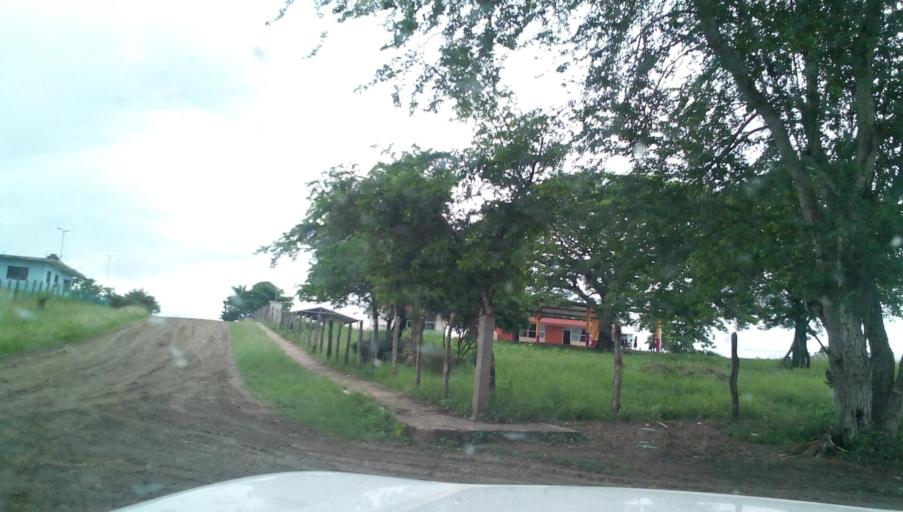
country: MX
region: Veracruz
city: Panuco
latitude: 21.8034
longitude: -98.1063
